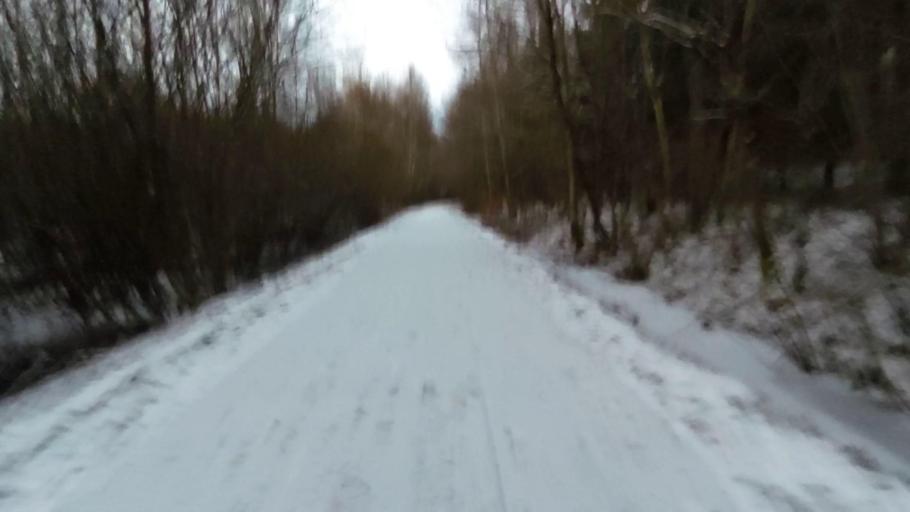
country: PL
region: West Pomeranian Voivodeship
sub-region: Powiat swidwinski
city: Polczyn-Zdroj
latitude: 53.7436
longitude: 16.0574
